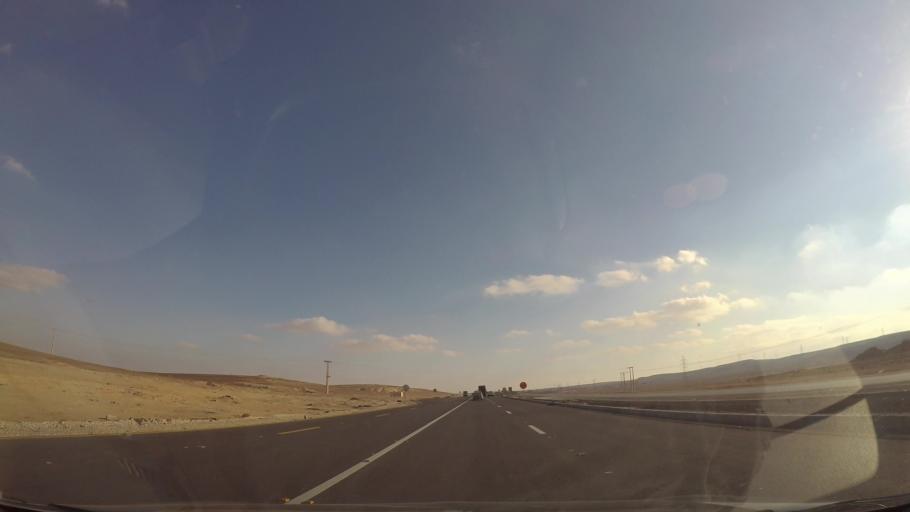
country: JO
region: Karak
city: Karak City
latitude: 31.1105
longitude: 36.0069
